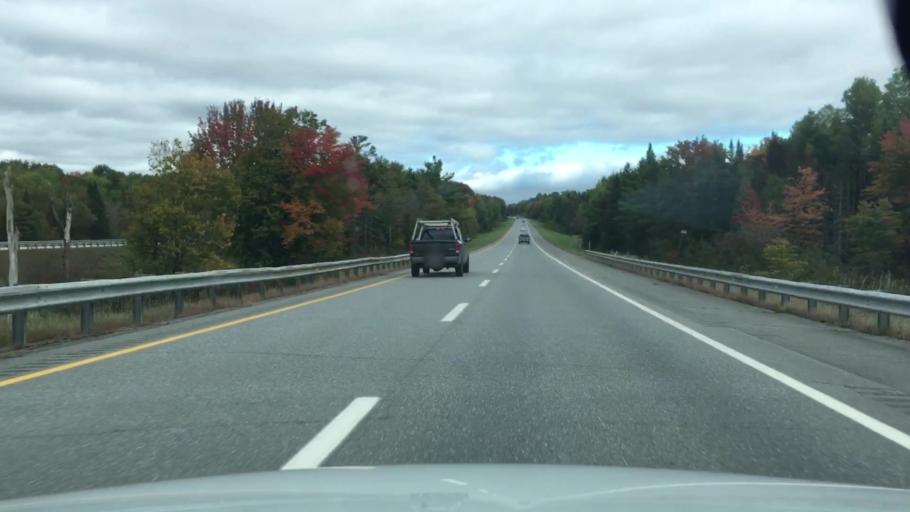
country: US
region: Maine
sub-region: Penobscot County
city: Carmel
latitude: 44.7756
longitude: -69.0443
